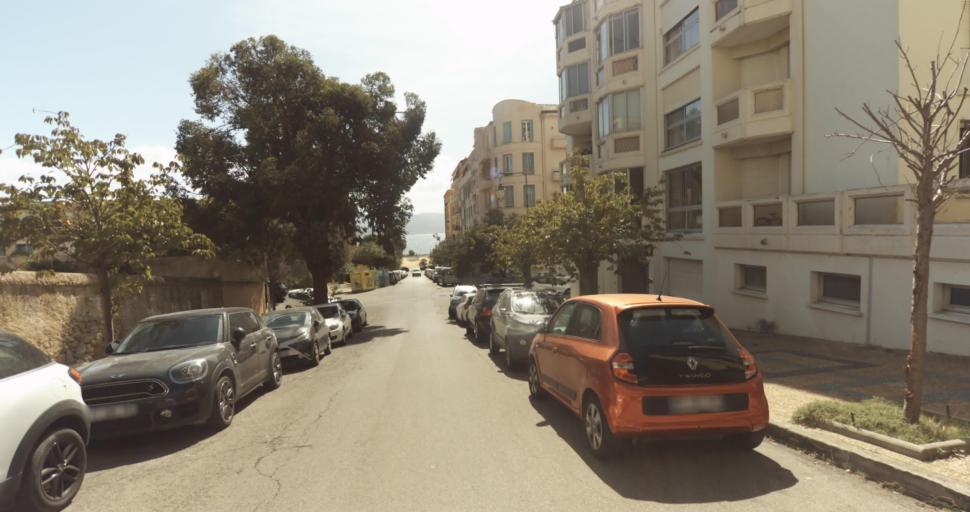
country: FR
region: Corsica
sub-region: Departement de la Corse-du-Sud
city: Ajaccio
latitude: 41.9154
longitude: 8.7284
